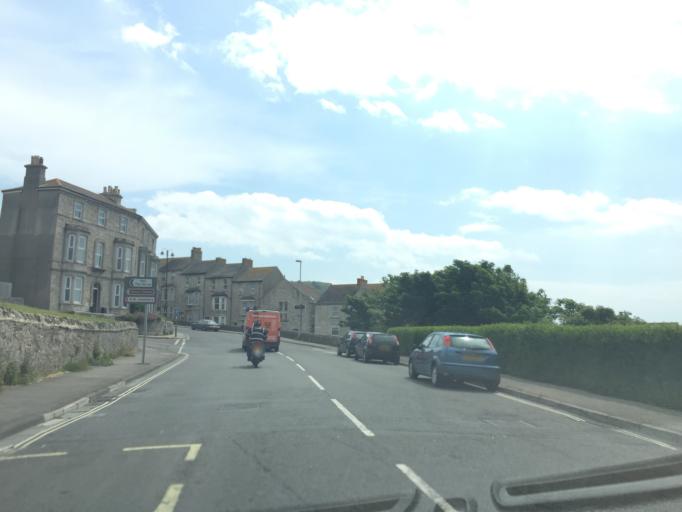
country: GB
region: England
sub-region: Dorset
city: Fortuneswell
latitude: 50.5622
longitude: -2.4467
